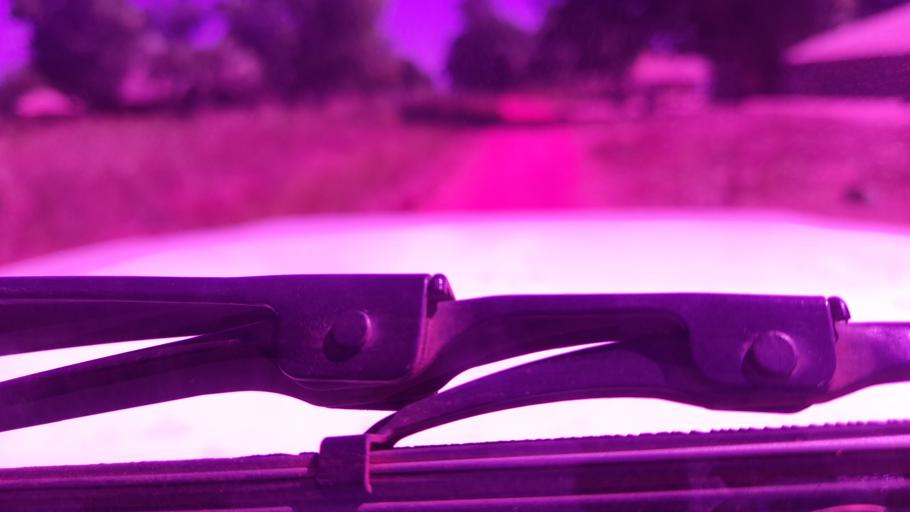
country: GW
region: Oio
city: Bissora
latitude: 12.3909
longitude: -15.6278
